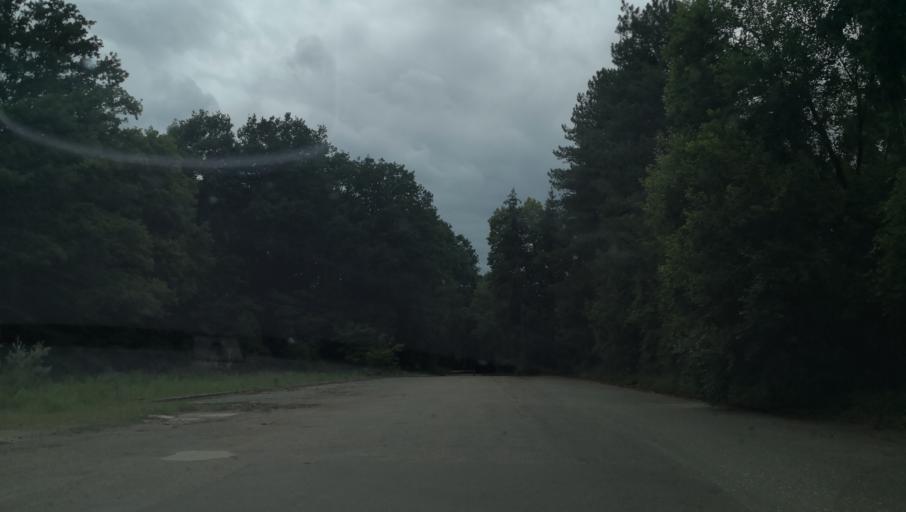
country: FR
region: Ile-de-France
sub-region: Departement des Yvelines
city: Guyancourt
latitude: 48.7816
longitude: 2.0853
